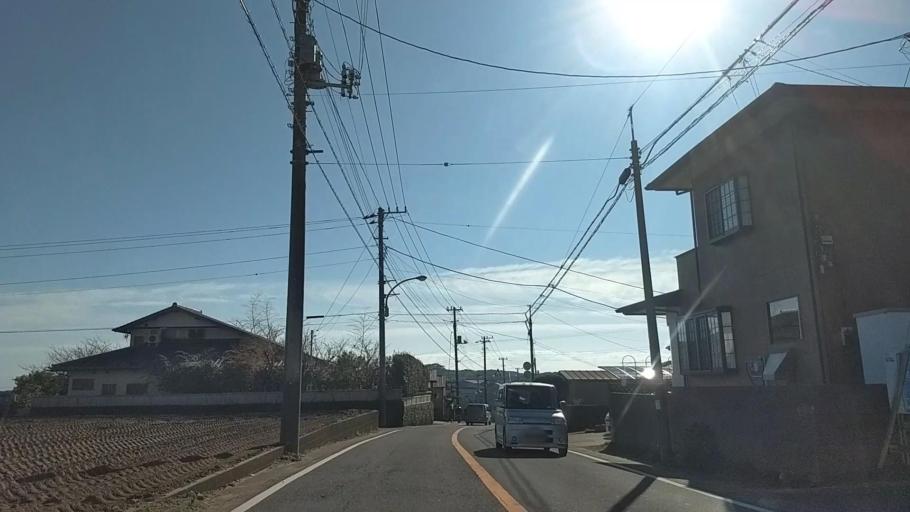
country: JP
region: Chiba
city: Hasaki
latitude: 35.7143
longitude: 140.8584
